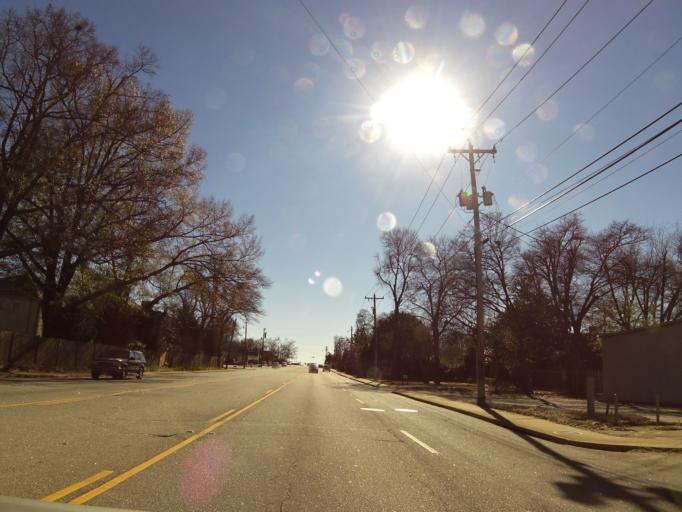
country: US
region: South Carolina
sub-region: Greenville County
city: Greenville
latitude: 34.8672
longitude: -82.4045
